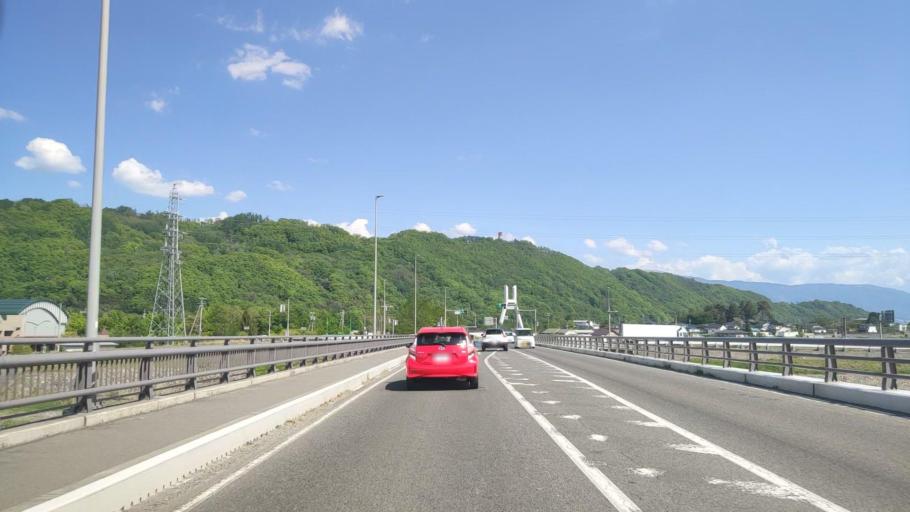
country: JP
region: Nagano
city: Matsumoto
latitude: 36.2692
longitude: 137.9380
